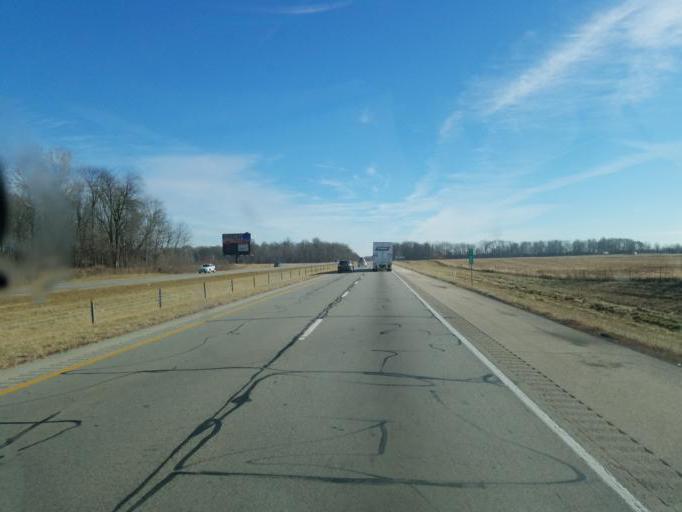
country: US
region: Indiana
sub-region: Henry County
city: New Castle
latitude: 39.8527
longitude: -85.3767
